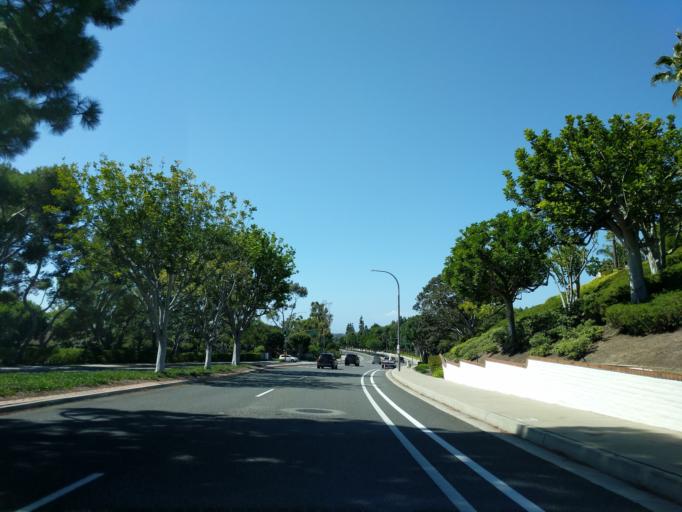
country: US
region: California
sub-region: Orange County
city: San Joaquin Hills
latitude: 33.6288
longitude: -117.8677
